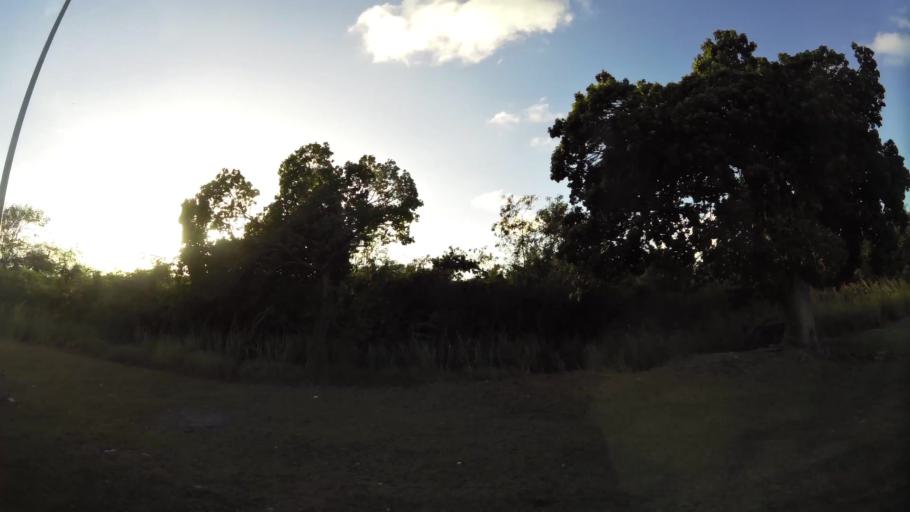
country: AG
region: Saint George
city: Piggotts
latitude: 17.1540
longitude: -61.7986
